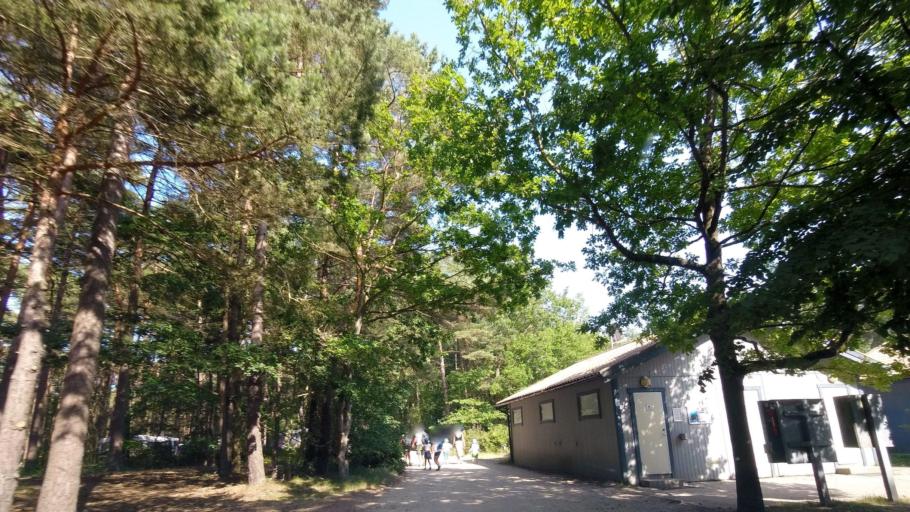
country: DE
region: Mecklenburg-Vorpommern
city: Wiek
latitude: 54.6717
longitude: 13.2975
